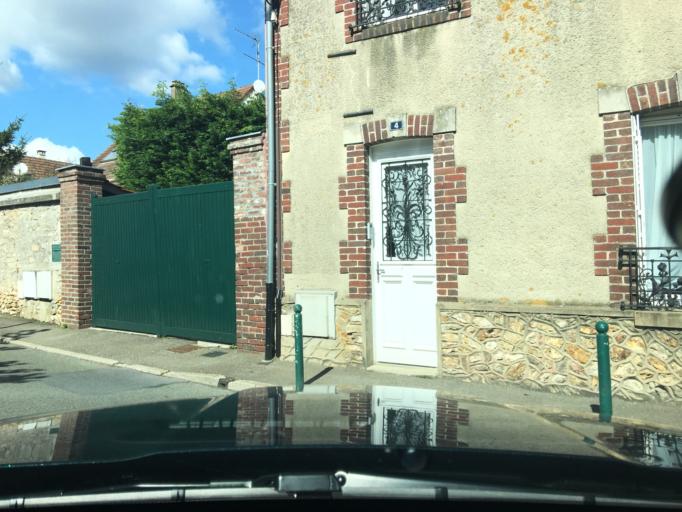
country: FR
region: Picardie
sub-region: Departement de l'Oise
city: Plailly
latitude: 49.1041
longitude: 2.5822
